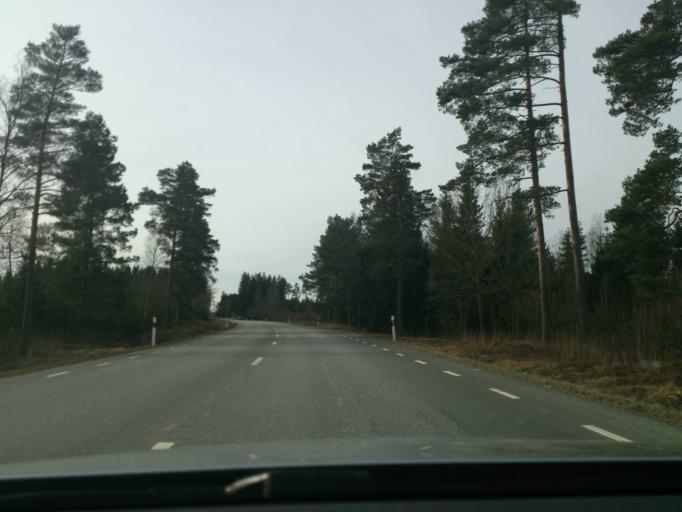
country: SE
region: Kronoberg
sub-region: Alvesta Kommun
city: Moheda
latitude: 56.9509
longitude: 14.5648
